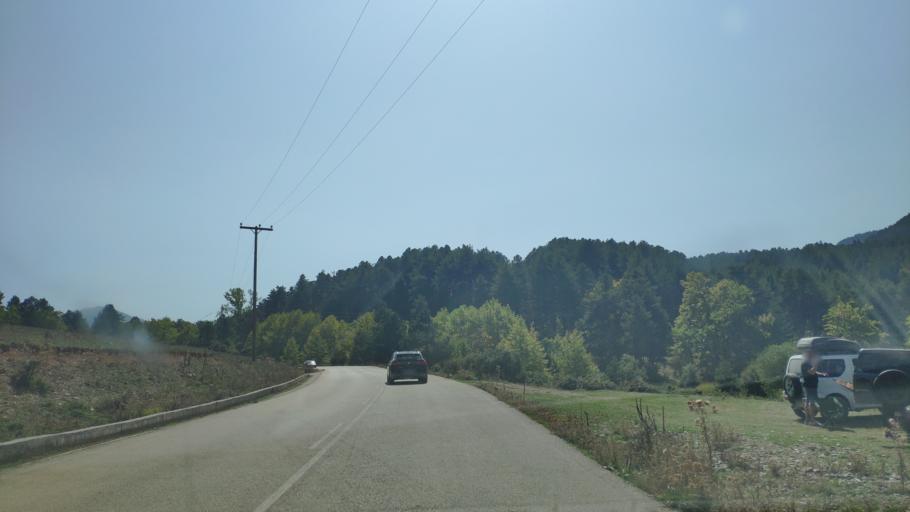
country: GR
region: West Greece
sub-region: Nomos Achaias
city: Kalavryta
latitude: 37.9255
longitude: 22.2927
